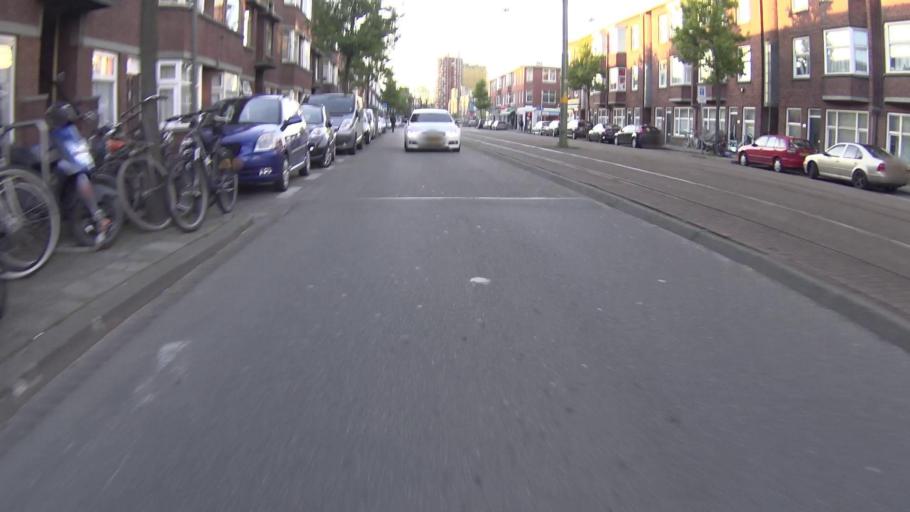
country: NL
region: South Holland
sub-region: Gemeente Rijswijk
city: Rijswijk
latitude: 52.0614
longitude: 4.3264
